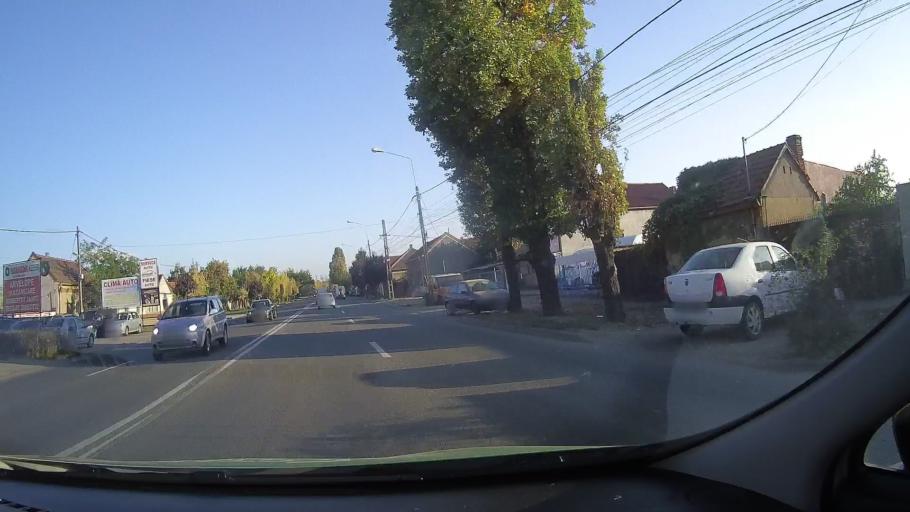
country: RO
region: Bihor
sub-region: Comuna Biharea
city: Oradea
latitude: 47.0926
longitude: 21.9057
